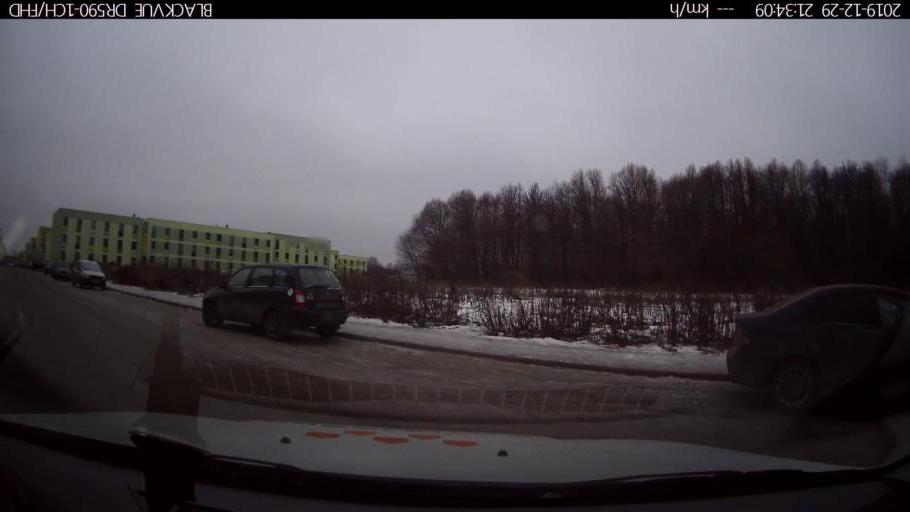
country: RU
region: Nizjnij Novgorod
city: Afonino
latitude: 56.2159
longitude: 44.0173
